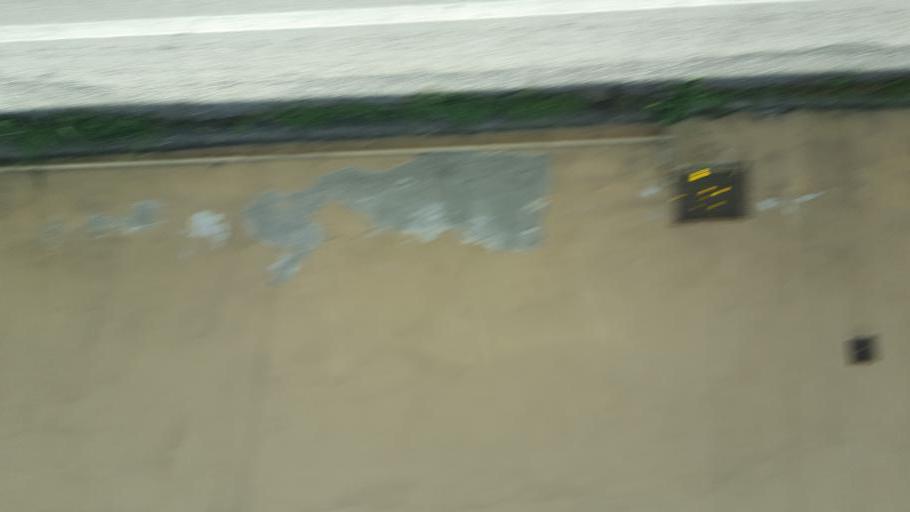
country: IT
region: Tuscany
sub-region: Provincia di Lucca
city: Capannori
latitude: 43.8623
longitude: 10.5419
